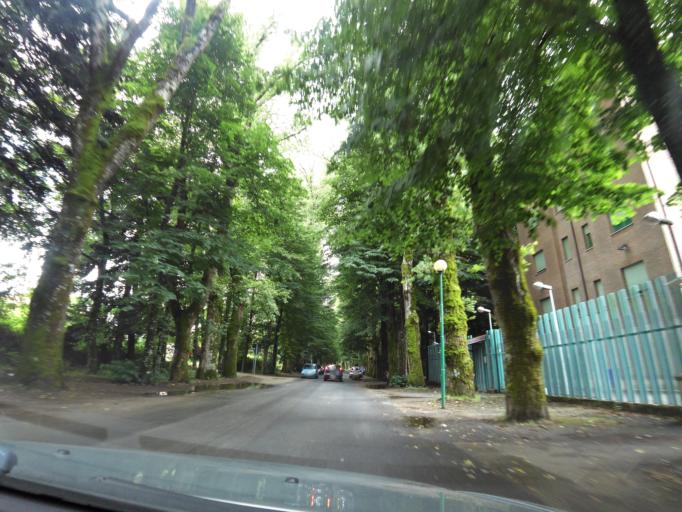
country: IT
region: Calabria
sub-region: Provincia di Vibo-Valentia
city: Serra San Bruno
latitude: 38.5705
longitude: 16.3242
